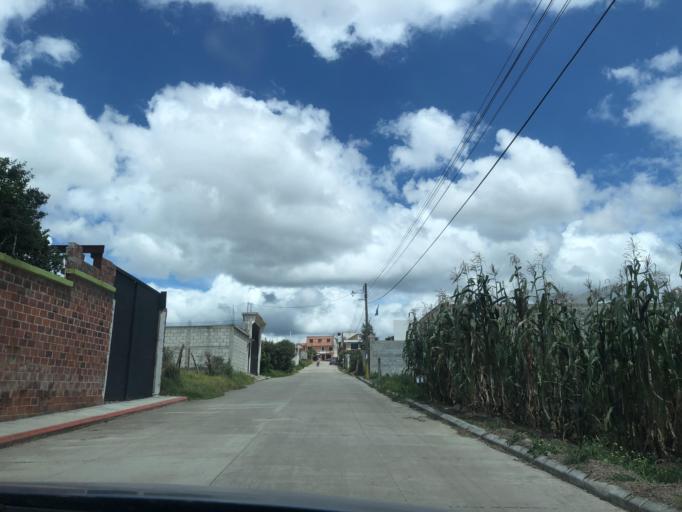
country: GT
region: Quetzaltenango
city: Quetzaltenango
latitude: 14.8397
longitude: -91.5444
